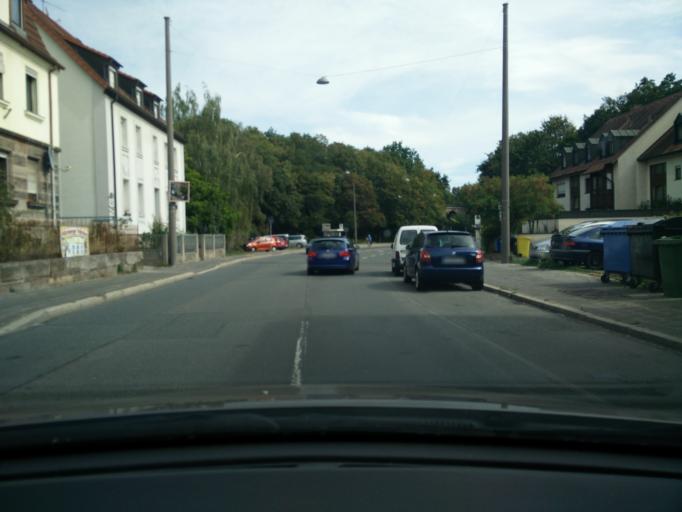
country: DE
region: Bavaria
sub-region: Regierungsbezirk Mittelfranken
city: Seukendorf
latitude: 49.4877
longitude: 10.9289
